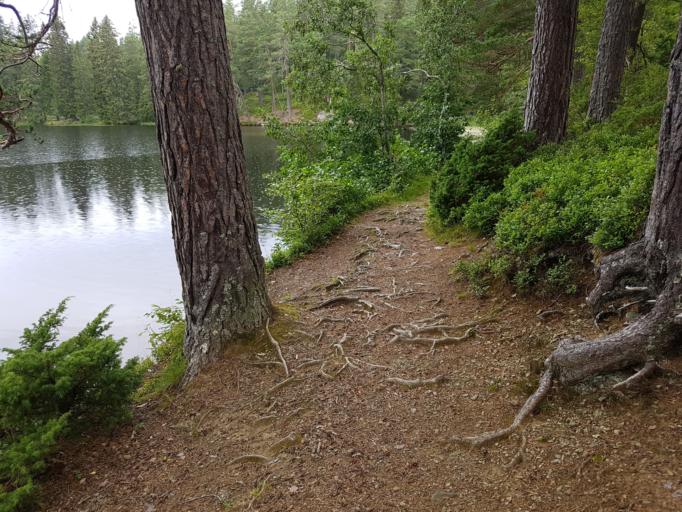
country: NO
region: Sor-Trondelag
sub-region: Trondheim
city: Trondheim
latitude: 63.4197
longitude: 10.3226
